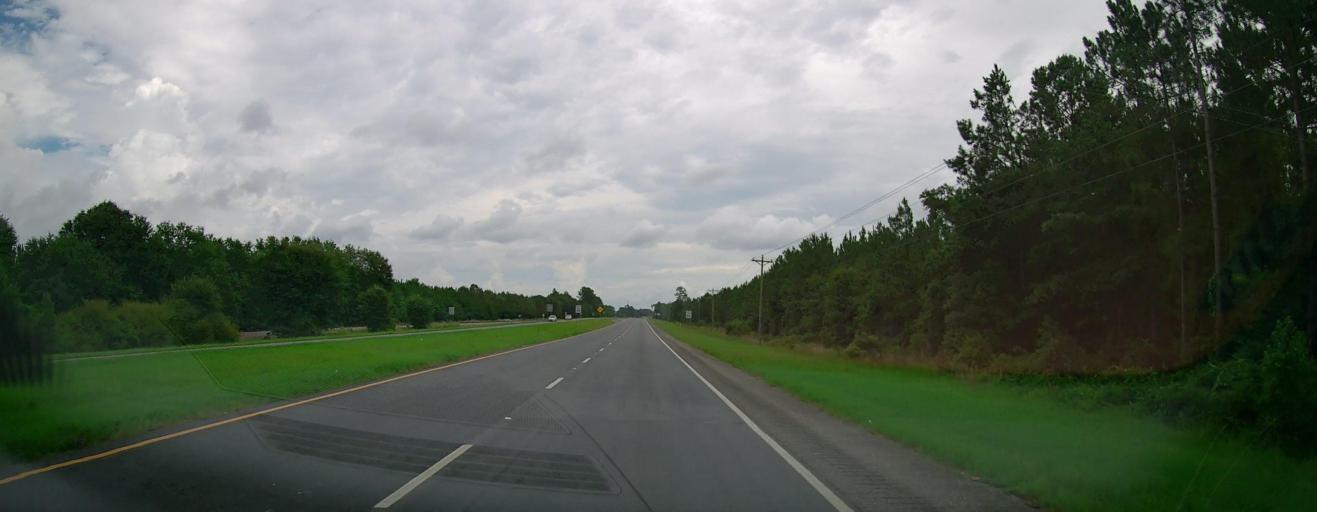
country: US
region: Georgia
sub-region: Dodge County
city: Eastman
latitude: 32.1083
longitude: -83.0885
